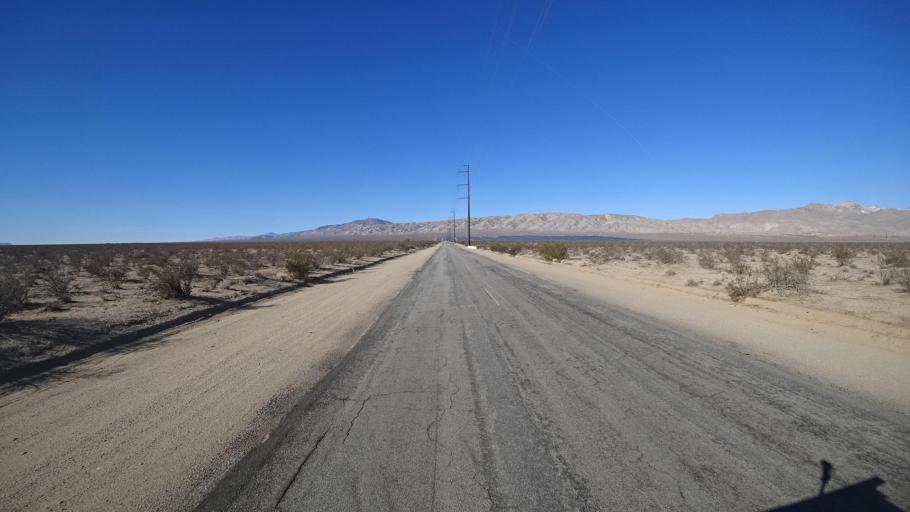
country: US
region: California
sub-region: Kern County
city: California City
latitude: 35.2001
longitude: -118.0367
